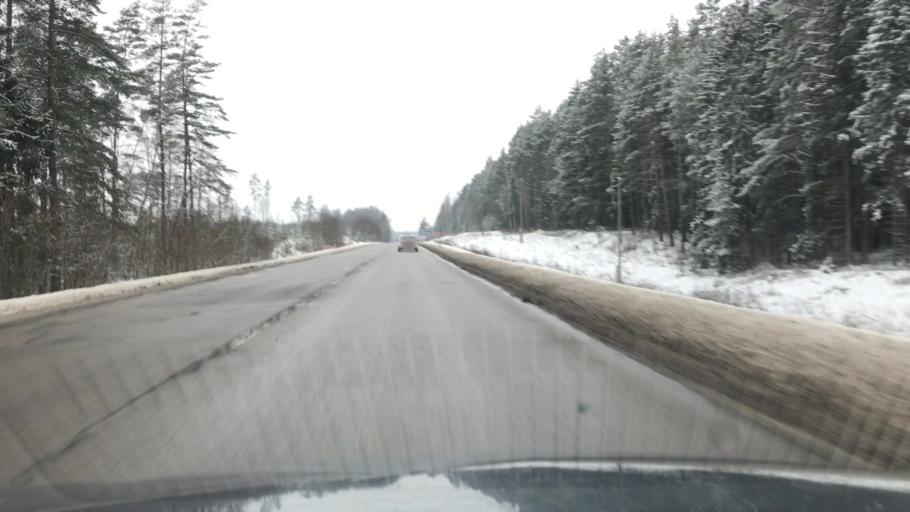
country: LV
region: Baldone
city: Baldone
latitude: 56.7576
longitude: 24.3271
